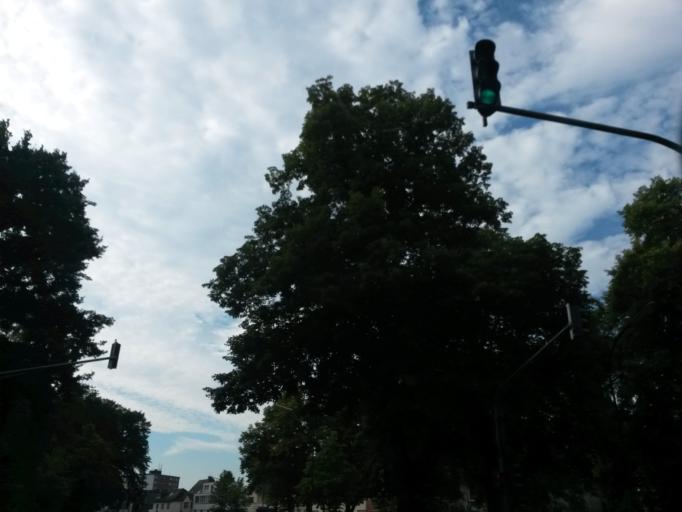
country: DE
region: North Rhine-Westphalia
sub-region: Regierungsbezirk Koln
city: Troisdorf
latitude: 50.8171
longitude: 7.1625
